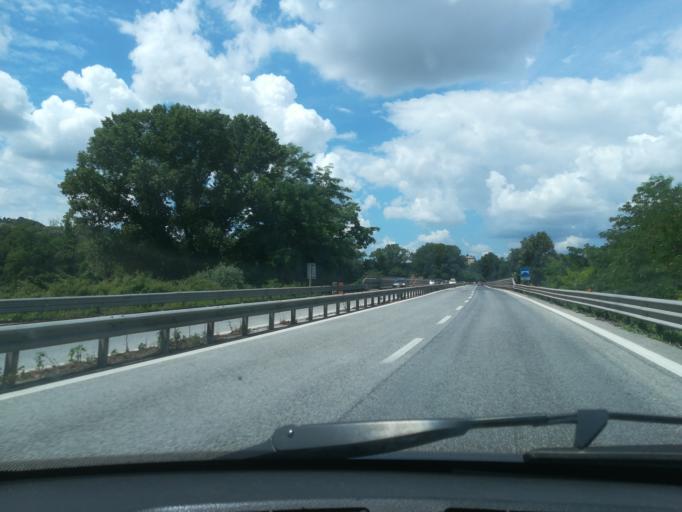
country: IT
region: The Marches
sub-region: Provincia di Macerata
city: Corridonia
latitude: 43.2656
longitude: 13.5411
